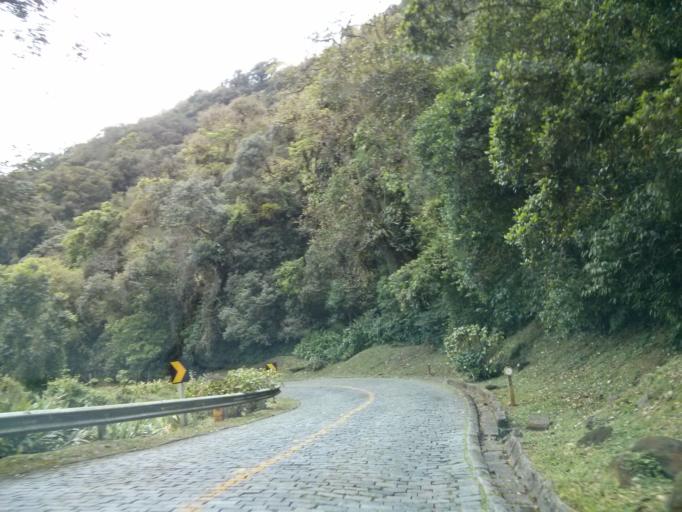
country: BR
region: Parana
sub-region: Campina Grande Do Sul
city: Campina Grande do Sul
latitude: -25.3455
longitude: -48.8914
